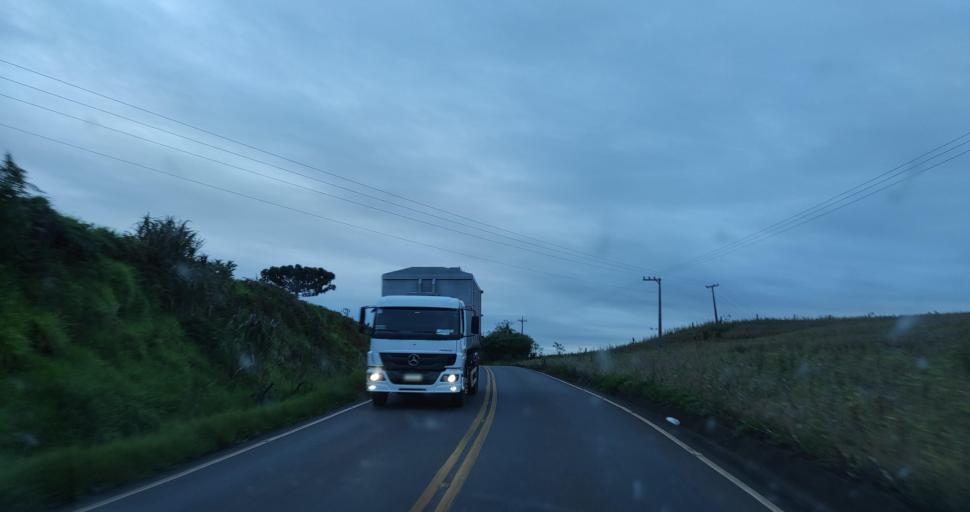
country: BR
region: Santa Catarina
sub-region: Xanxere
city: Xanxere
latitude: -26.7284
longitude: -52.4039
